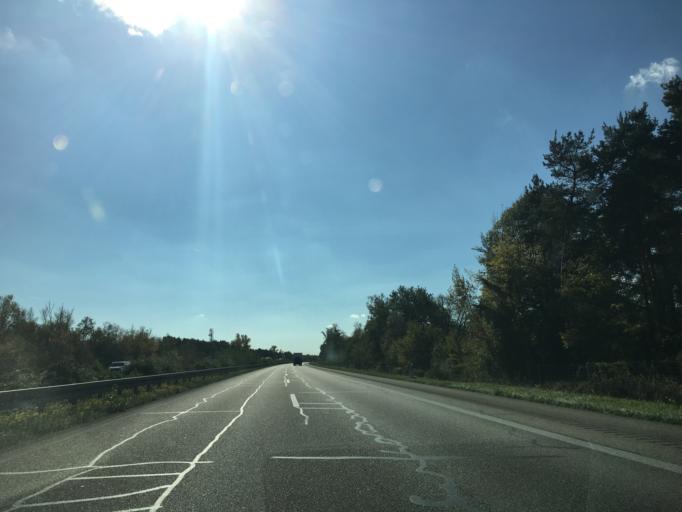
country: FR
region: Alsace
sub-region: Departement du Haut-Rhin
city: Blodelsheim
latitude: 47.8959
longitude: 7.5845
